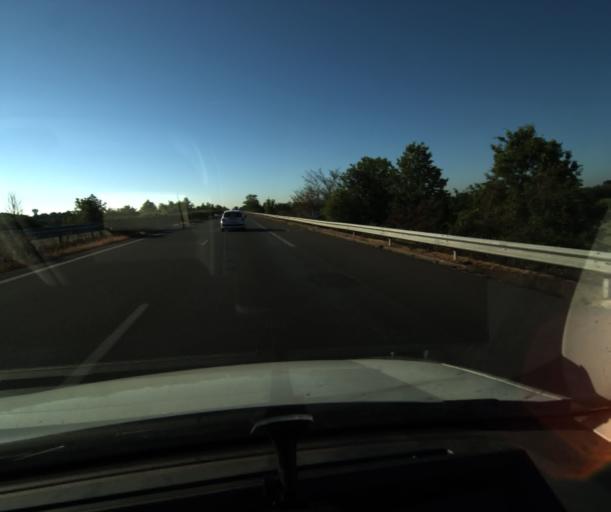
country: FR
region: Midi-Pyrenees
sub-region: Departement du Tarn-et-Garonne
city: Saint-Porquier
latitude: 44.0388
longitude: 1.1527
